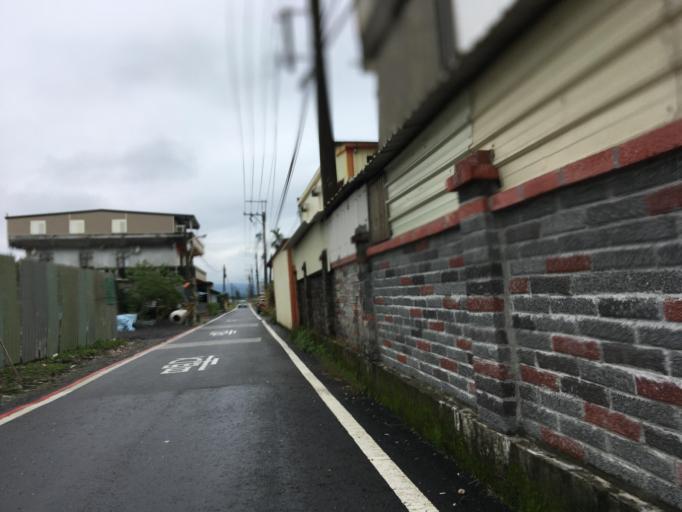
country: TW
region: Taiwan
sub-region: Yilan
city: Yilan
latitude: 24.6662
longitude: 121.7435
